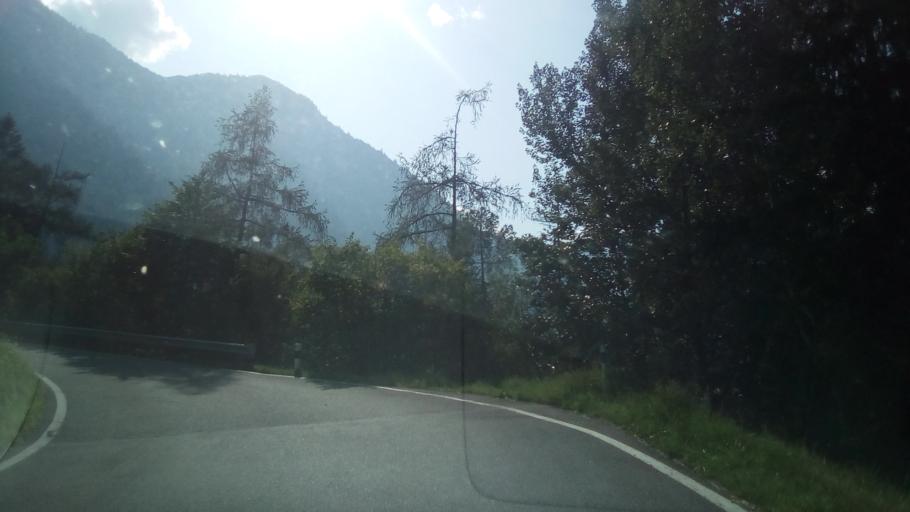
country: CH
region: Valais
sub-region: Martigny District
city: Martigny-Combe
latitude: 46.0701
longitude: 7.0753
